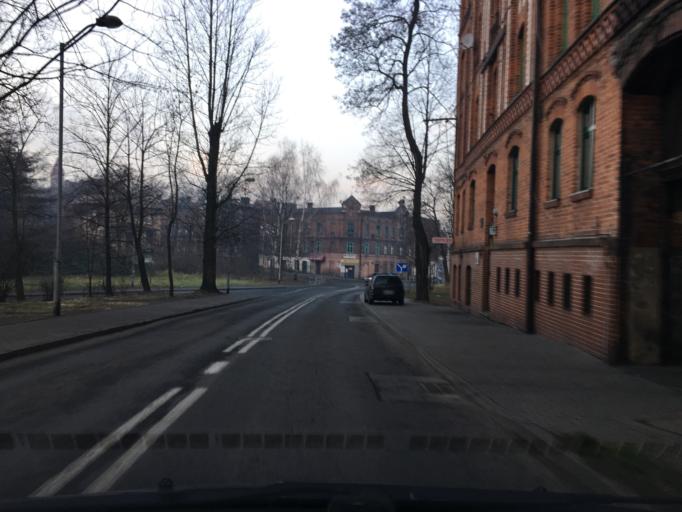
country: PL
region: Silesian Voivodeship
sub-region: Swietochlowice
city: Swietochlowice
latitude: 50.3201
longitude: 18.8785
